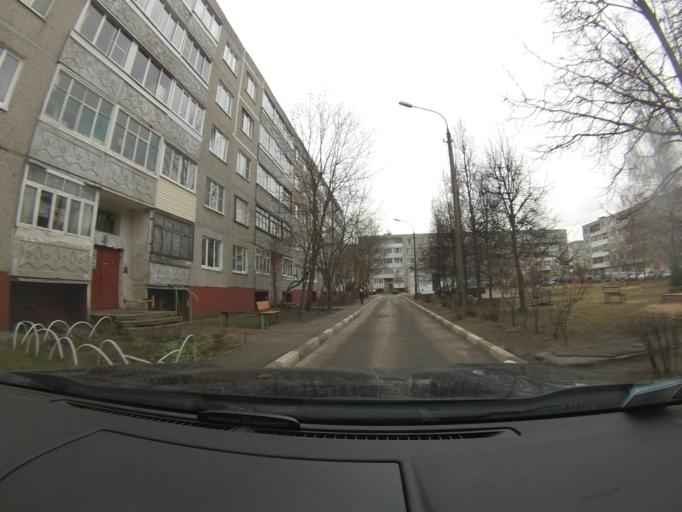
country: RU
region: Moskovskaya
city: Lopatinskiy
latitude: 55.3363
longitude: 38.7124
